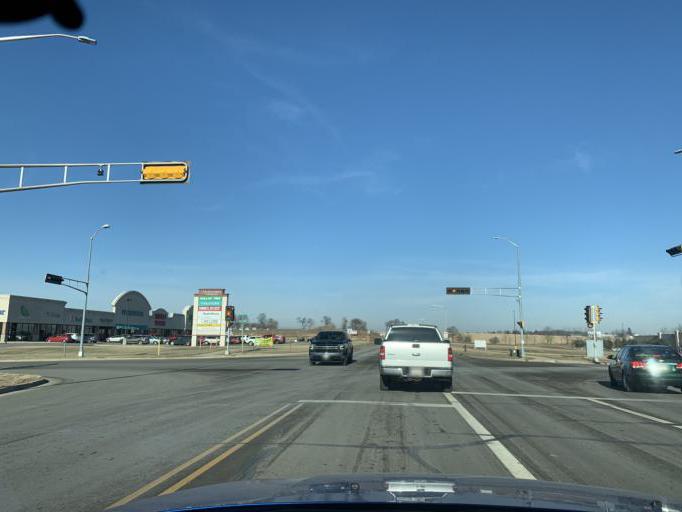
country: US
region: Wisconsin
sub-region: Green County
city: Monroe
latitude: 42.6073
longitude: -89.6661
